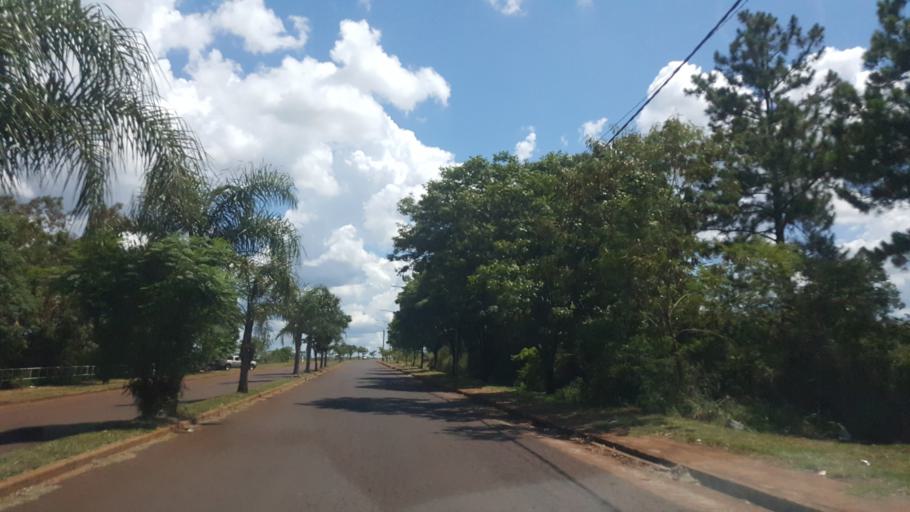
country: AR
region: Misiones
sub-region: Departamento de Capital
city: Posadas
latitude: -27.3753
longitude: -55.9613
